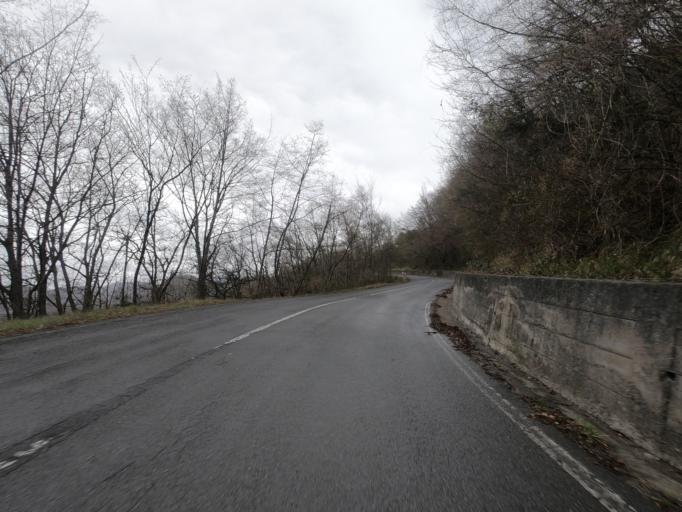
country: IT
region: Liguria
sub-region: Provincia di Imperia
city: Cesio
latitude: 44.0245
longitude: 7.9923
